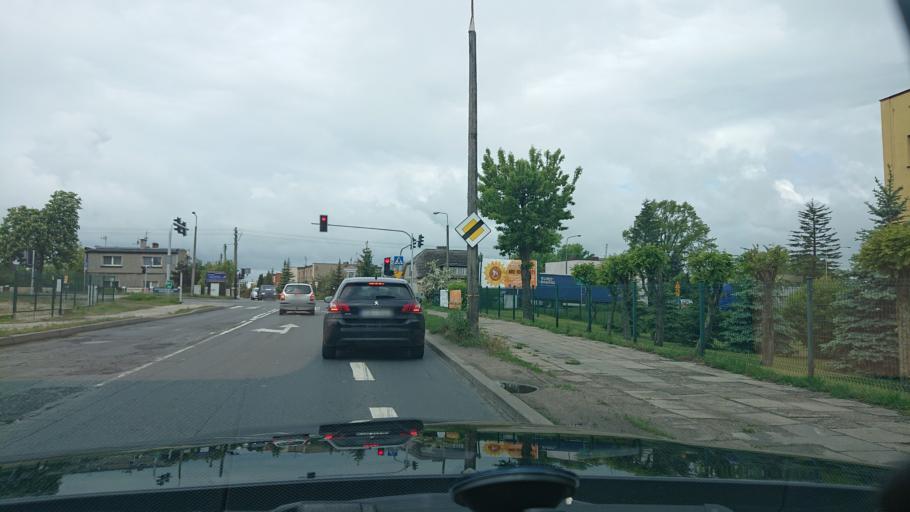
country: PL
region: Greater Poland Voivodeship
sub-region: Powiat gnieznienski
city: Gniezno
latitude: 52.5123
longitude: 17.5960
